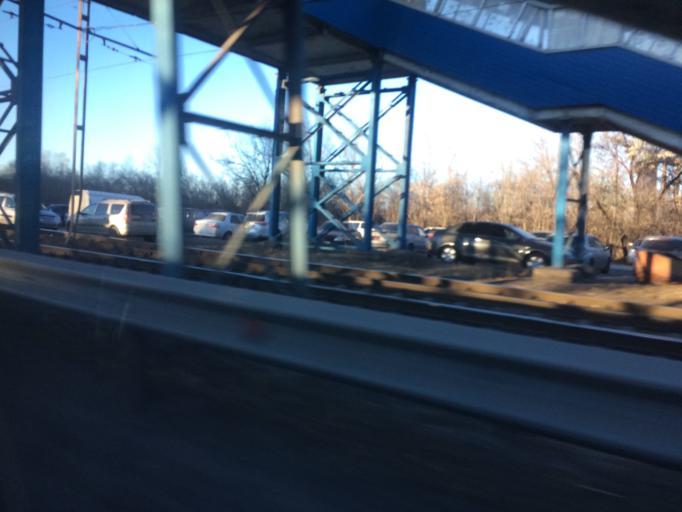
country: RU
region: Chelyabinsk
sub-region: Gorod Magnitogorsk
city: Magnitogorsk
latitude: 53.4024
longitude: 59.0265
